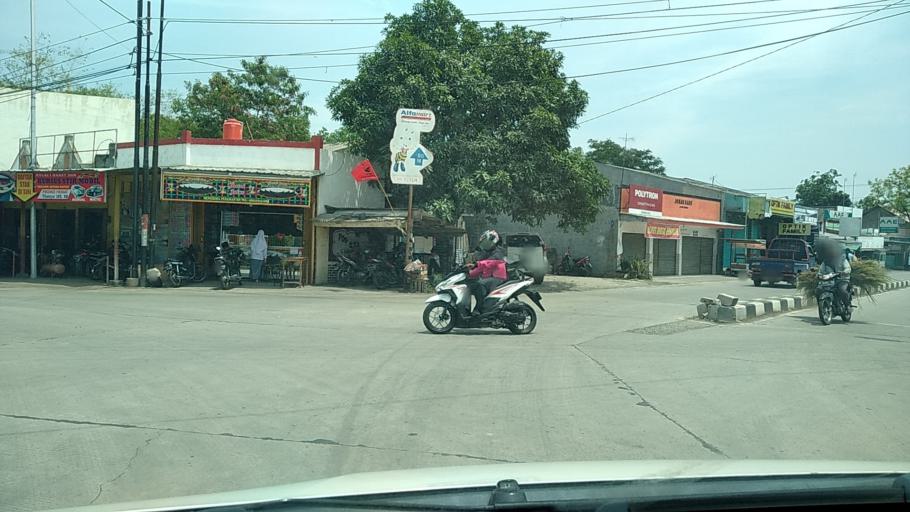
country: ID
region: Central Java
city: Mranggen
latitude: -7.0579
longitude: 110.4710
